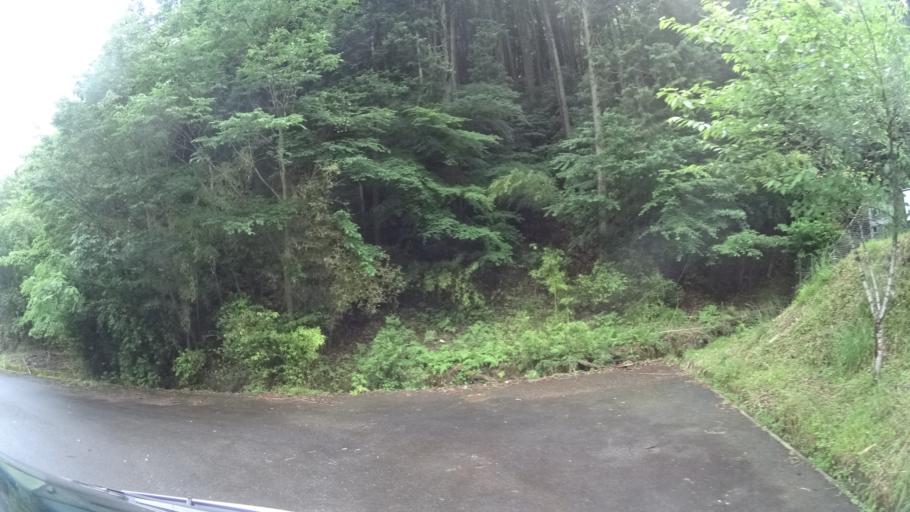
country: JP
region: Kyoto
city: Ayabe
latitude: 35.3952
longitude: 135.2352
